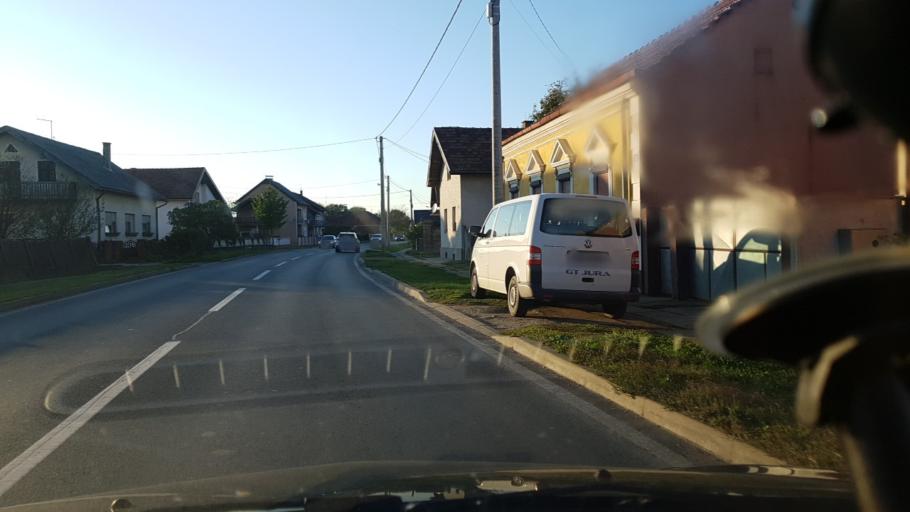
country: HR
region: Koprivnicko-Krizevacka
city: Virje
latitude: 46.0669
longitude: 16.9811
